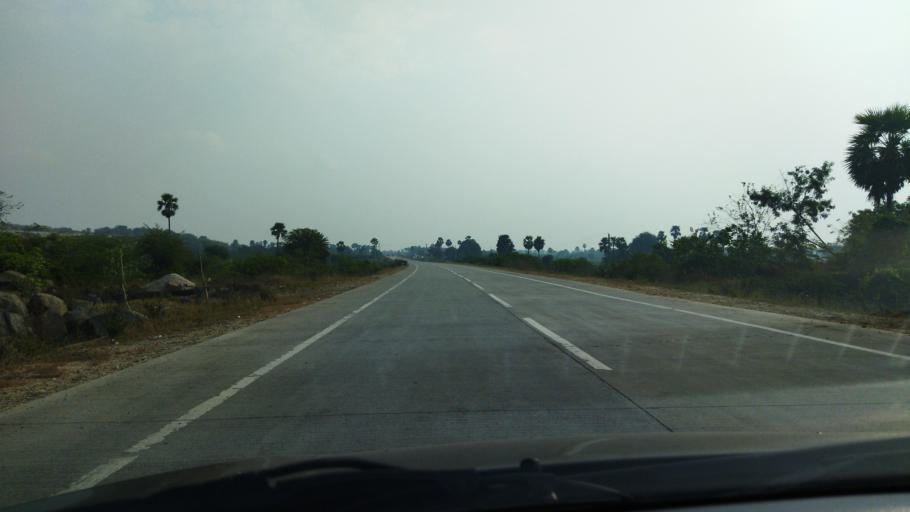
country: IN
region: Telangana
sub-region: Nalgonda
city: Nalgonda
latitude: 17.1795
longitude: 79.4081
